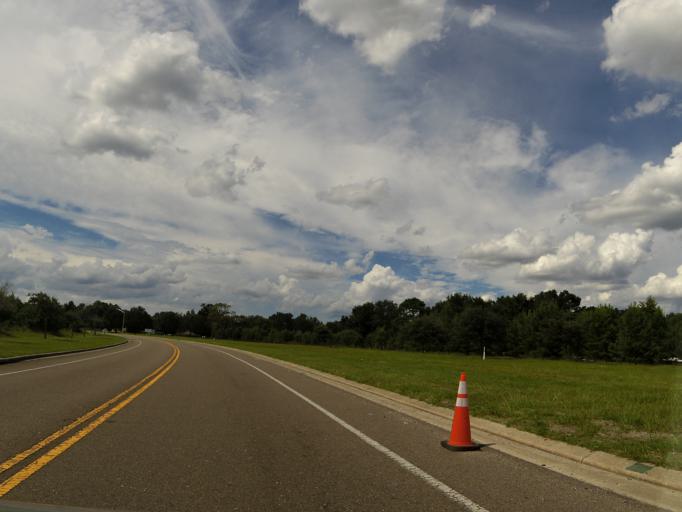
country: US
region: Florida
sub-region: Duval County
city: Jacksonville
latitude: 30.4272
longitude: -81.6360
